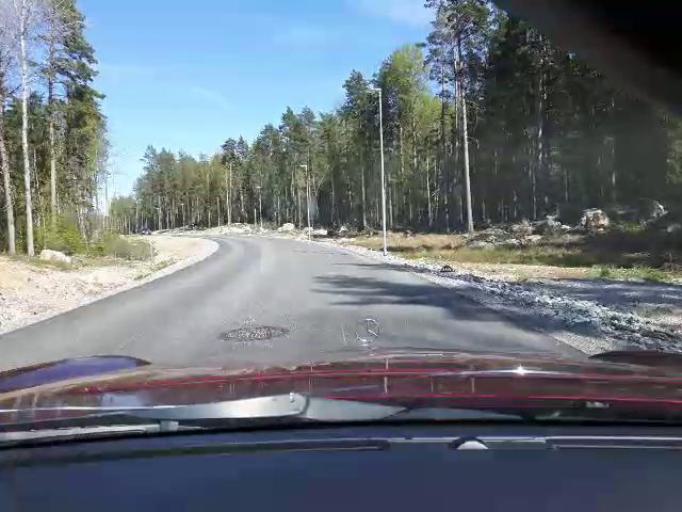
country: SE
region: OErebro
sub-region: Orebro Kommun
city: Orebro
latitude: 59.3038
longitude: 15.2488
